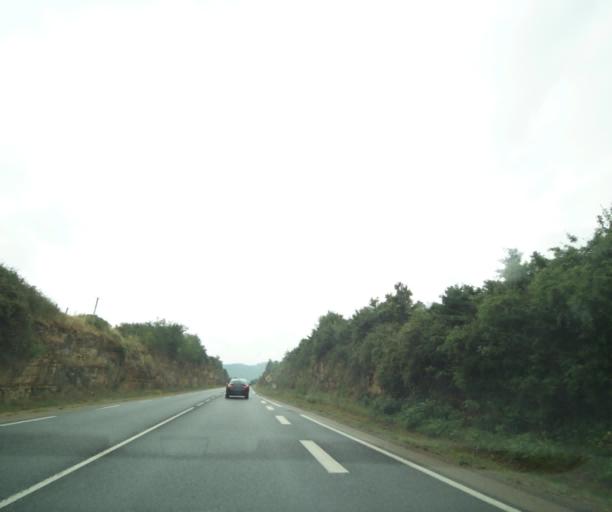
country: FR
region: Midi-Pyrenees
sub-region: Departement de l'Aveyron
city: Laissac
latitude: 44.3835
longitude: 2.8283
